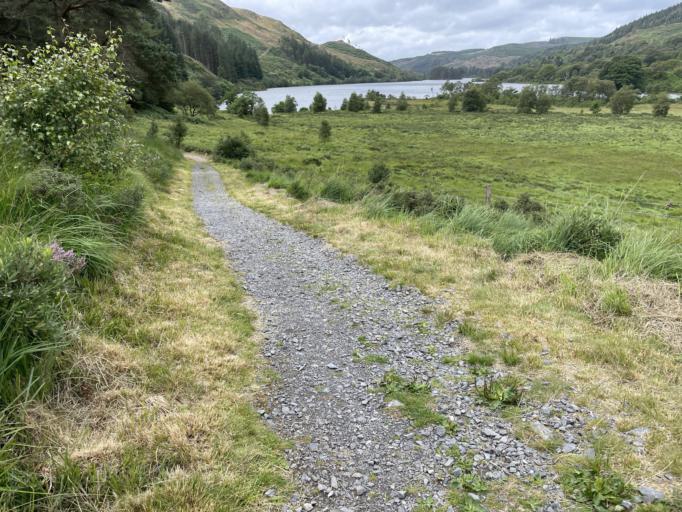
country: GB
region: Scotland
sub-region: Dumfries and Galloway
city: Newton Stewart
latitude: 55.0900
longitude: -4.4696
